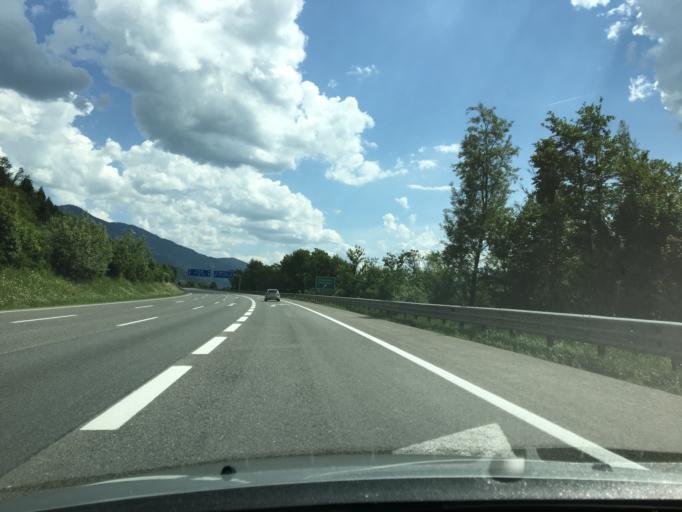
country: AT
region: Salzburg
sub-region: Politischer Bezirk Sankt Johann im Pongau
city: Pfarrwerfen
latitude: 47.4462
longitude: 13.2179
